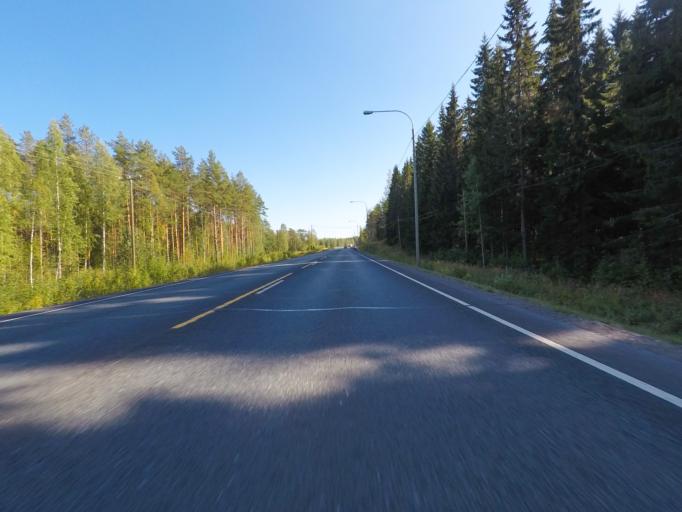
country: FI
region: Northern Savo
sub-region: Varkaus
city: Leppaevirta
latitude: 62.5356
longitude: 27.6475
